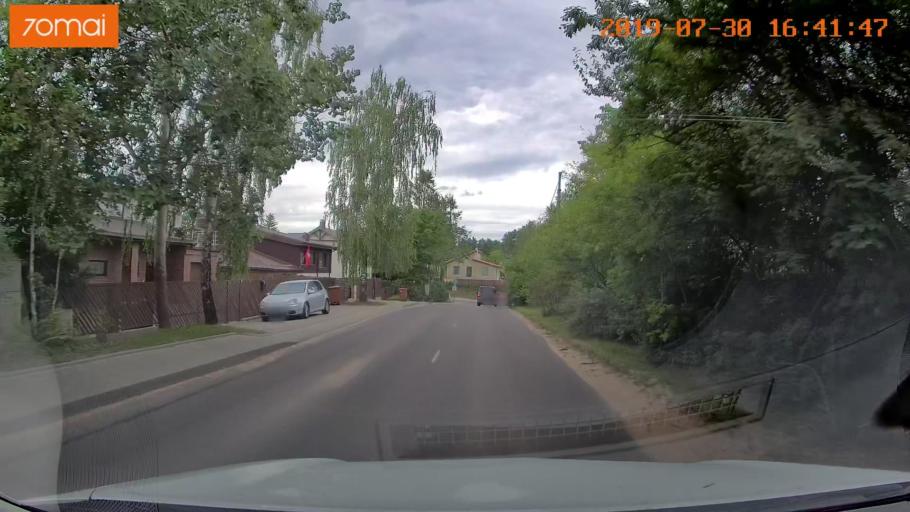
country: LT
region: Vilnius County
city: Rasos
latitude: 54.7137
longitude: 25.3519
